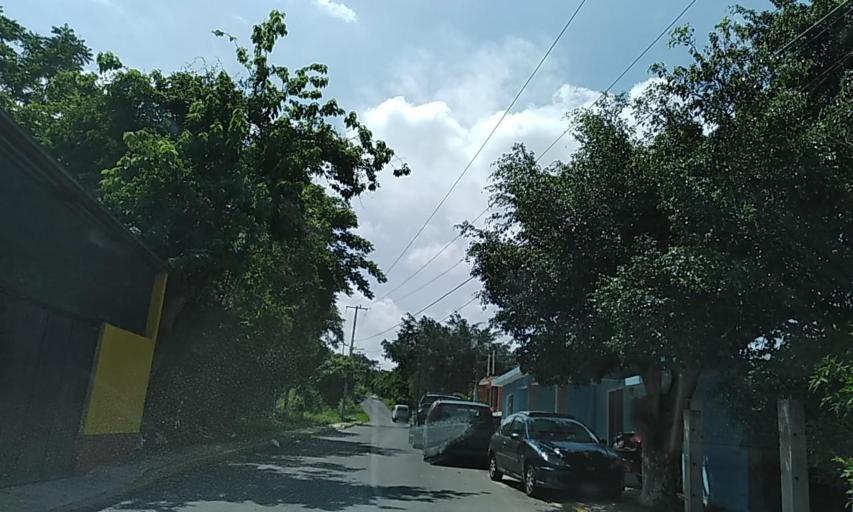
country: MX
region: Veracruz
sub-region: Emiliano Zapata
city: Dos Rios
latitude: 19.4373
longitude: -96.7784
